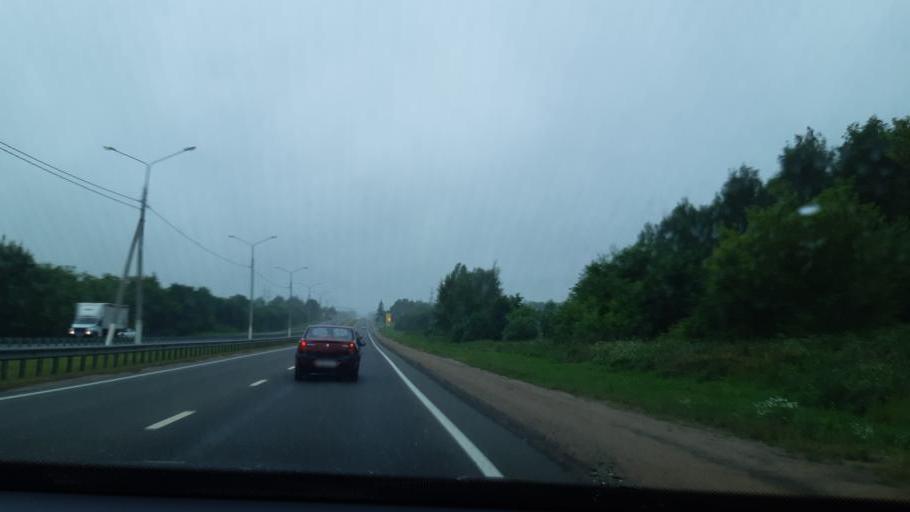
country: RU
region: Smolensk
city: Talashkino
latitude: 54.6529
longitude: 32.1661
